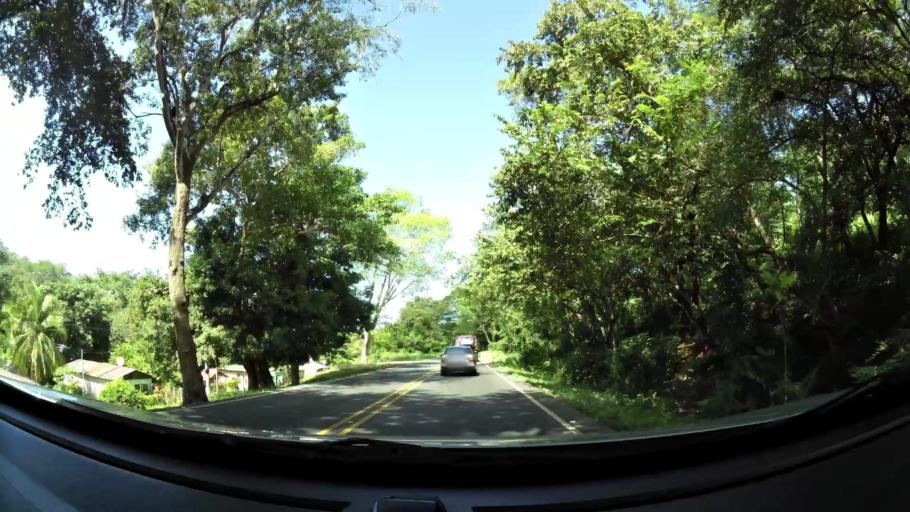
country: CR
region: Guanacaste
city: Juntas
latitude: 10.3102
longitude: -85.0407
